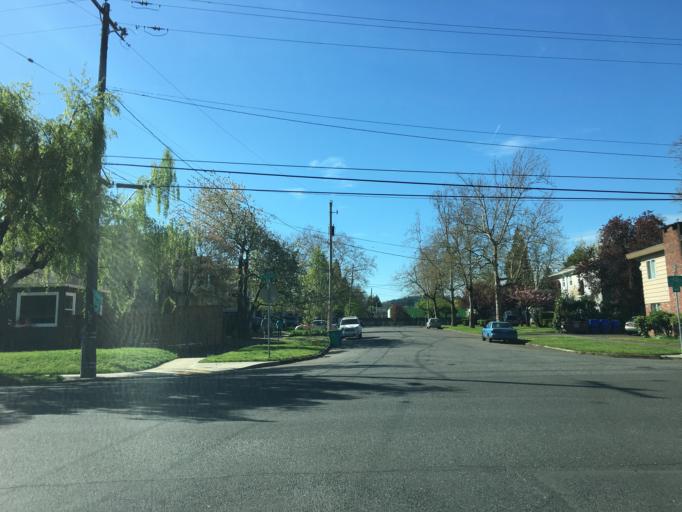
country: US
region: Oregon
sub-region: Multnomah County
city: Lents
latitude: 45.5373
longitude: -122.5894
